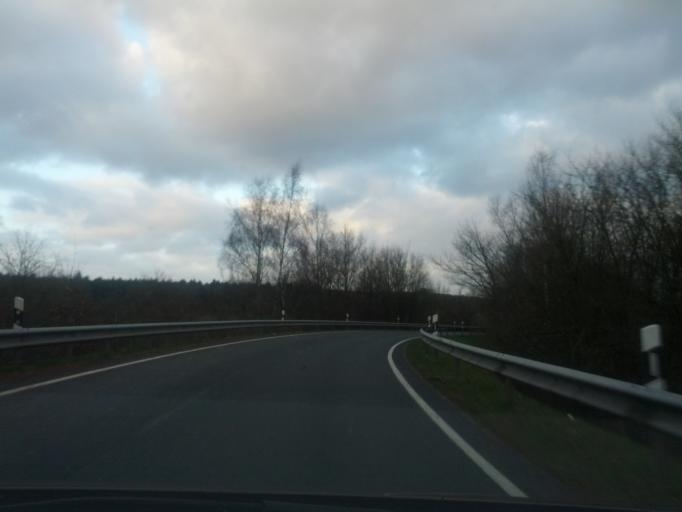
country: DE
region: Lower Saxony
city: Rotenburg
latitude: 53.1208
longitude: 9.3943
